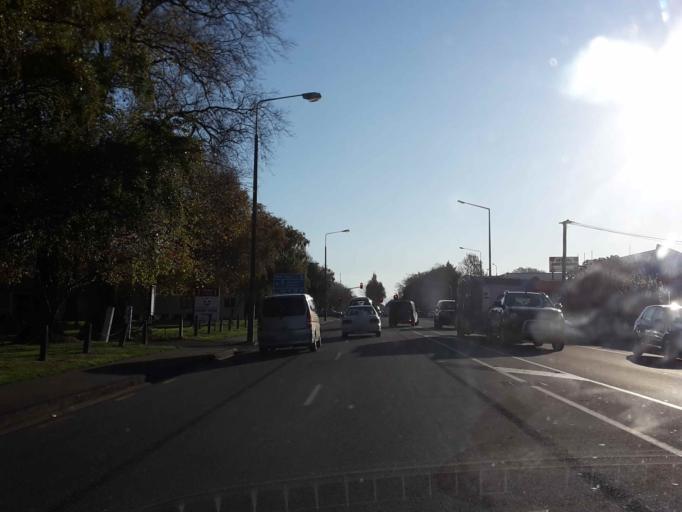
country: NZ
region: Canterbury
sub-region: Christchurch City
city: Christchurch
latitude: -43.5314
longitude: 172.5702
